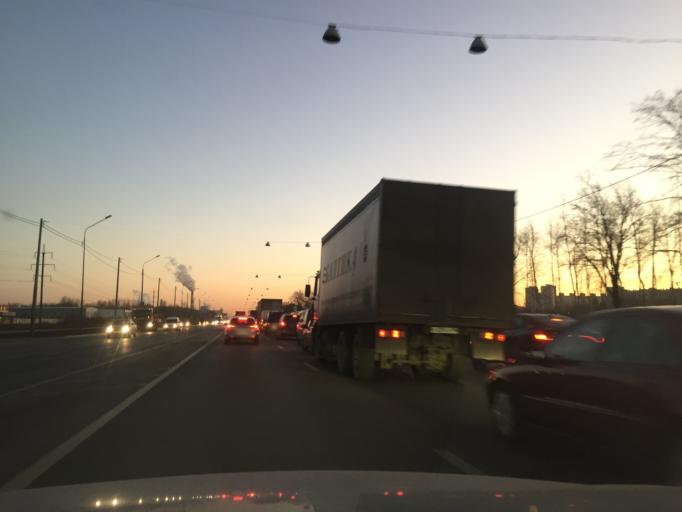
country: RU
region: St.-Petersburg
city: Obukhovo
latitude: 59.8557
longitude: 30.4234
